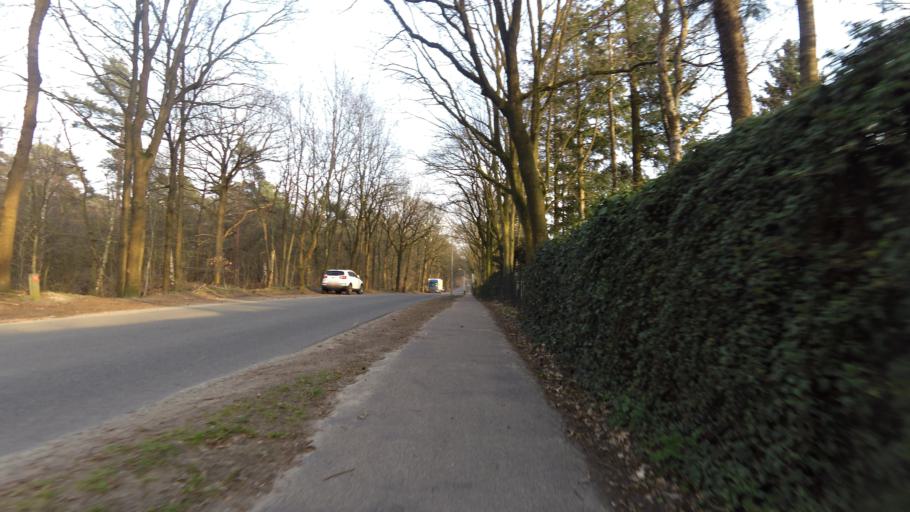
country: NL
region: Gelderland
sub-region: Gemeente Ede
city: Lunteren
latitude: 52.0992
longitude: 5.6430
